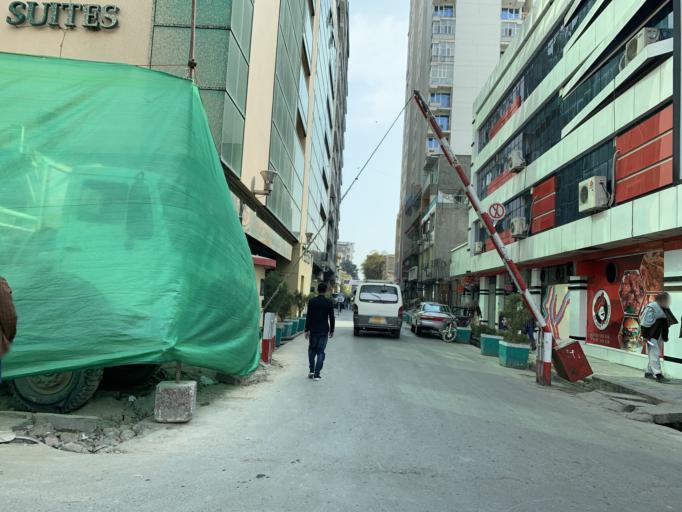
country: AF
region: Kabul
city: Kabul
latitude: 34.5323
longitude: 69.1650
